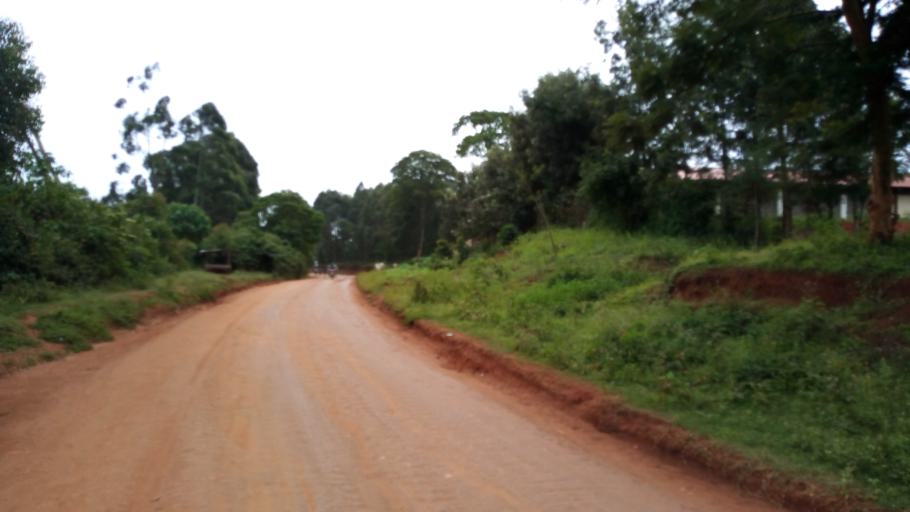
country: KE
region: Makueni
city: Wote
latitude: -1.6594
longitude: 37.4538
